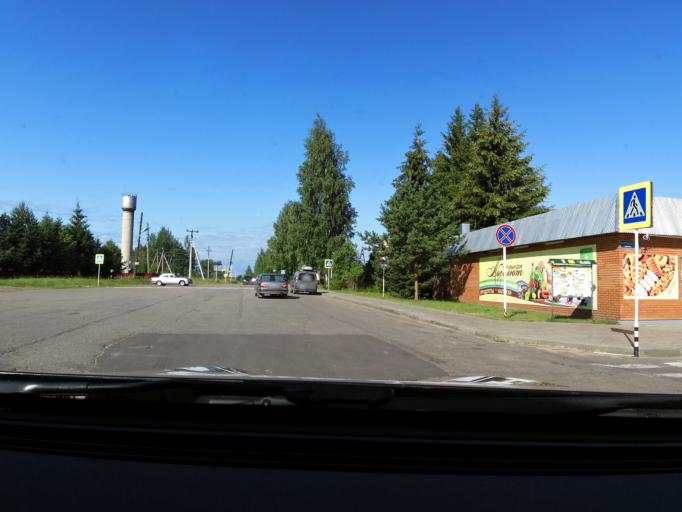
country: RU
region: Tverskaya
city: Zavidovo
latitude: 56.6104
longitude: 36.6193
